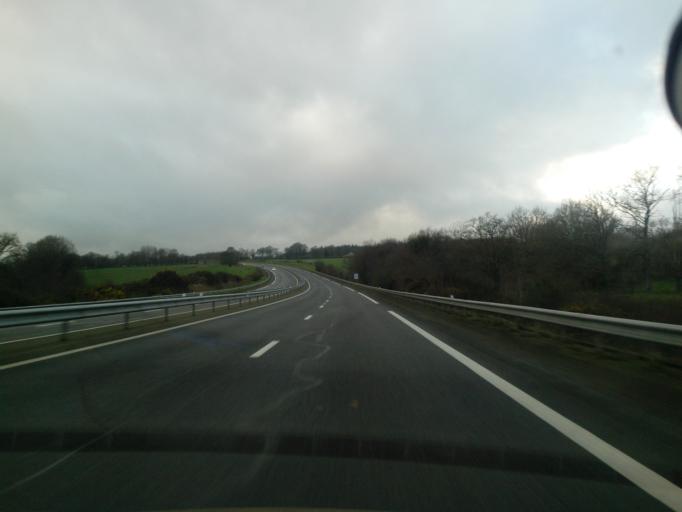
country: FR
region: Brittany
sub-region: Departement des Cotes-d'Armor
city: Plumaugat
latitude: 48.1968
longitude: -2.2670
